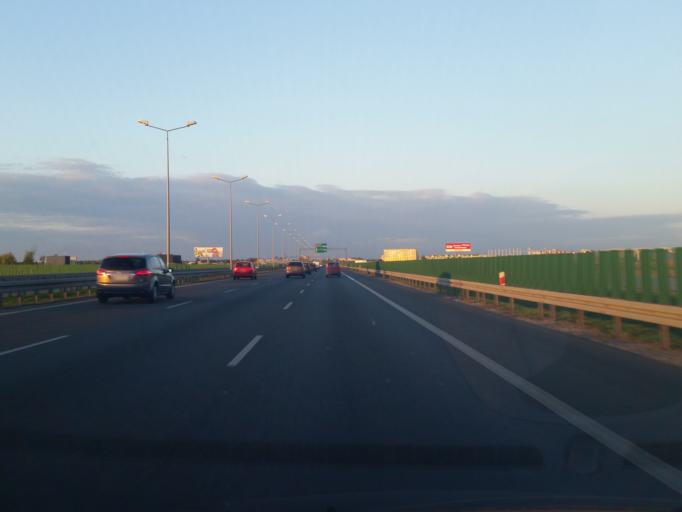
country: PL
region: Masovian Voivodeship
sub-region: Powiat warszawski zachodni
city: Babice
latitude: 52.2299
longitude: 20.8786
